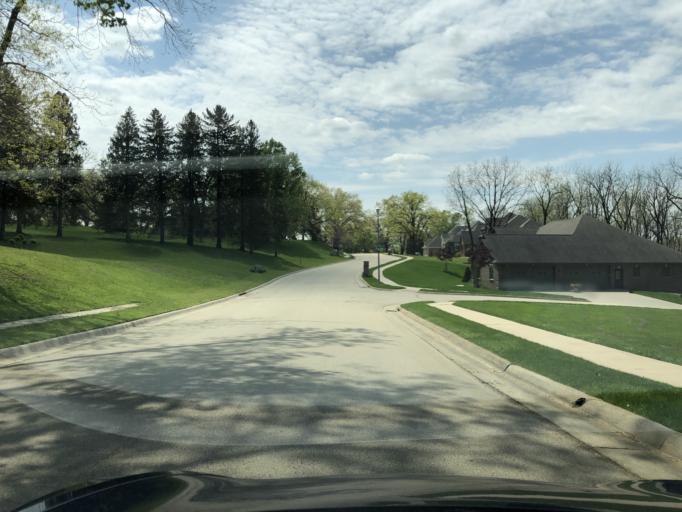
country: US
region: Iowa
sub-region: Dubuque County
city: Dubuque
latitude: 42.4773
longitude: -90.6629
